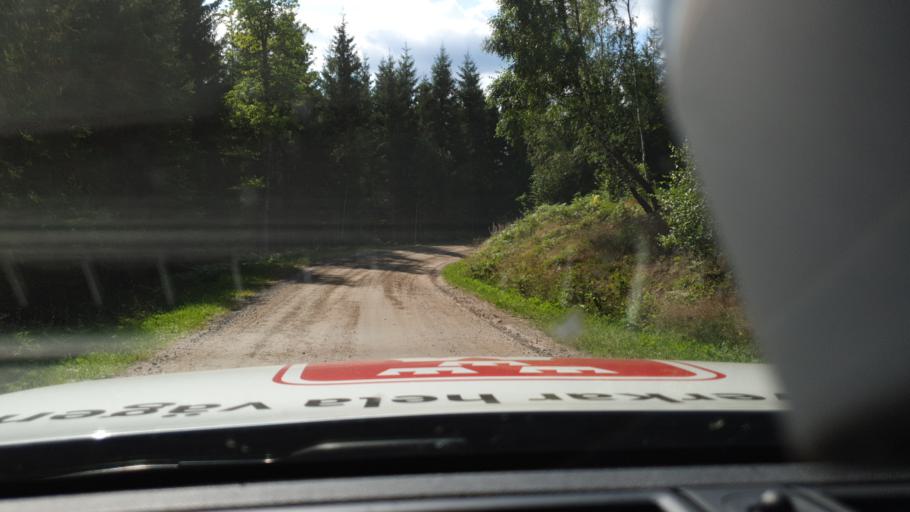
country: SE
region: Joenkoeping
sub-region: Gnosjo Kommun
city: Marieholm
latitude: 57.5545
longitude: 13.8320
